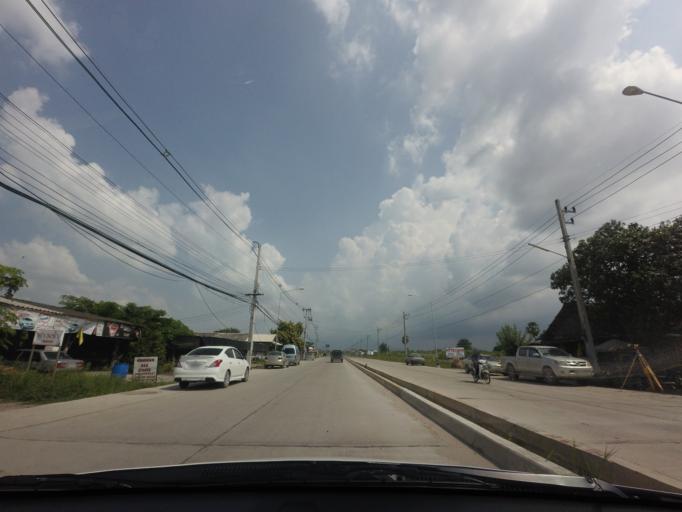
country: TH
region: Nakhon Pathom
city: Nakhon Chai Si
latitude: 13.8042
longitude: 100.1983
